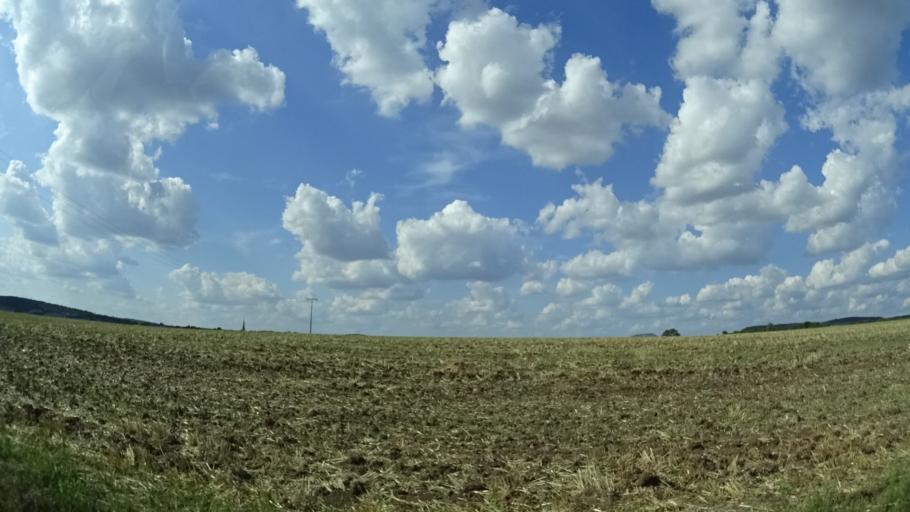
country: DE
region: Bavaria
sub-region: Regierungsbezirk Unterfranken
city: Trappstadt
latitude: 50.2859
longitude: 10.5714
